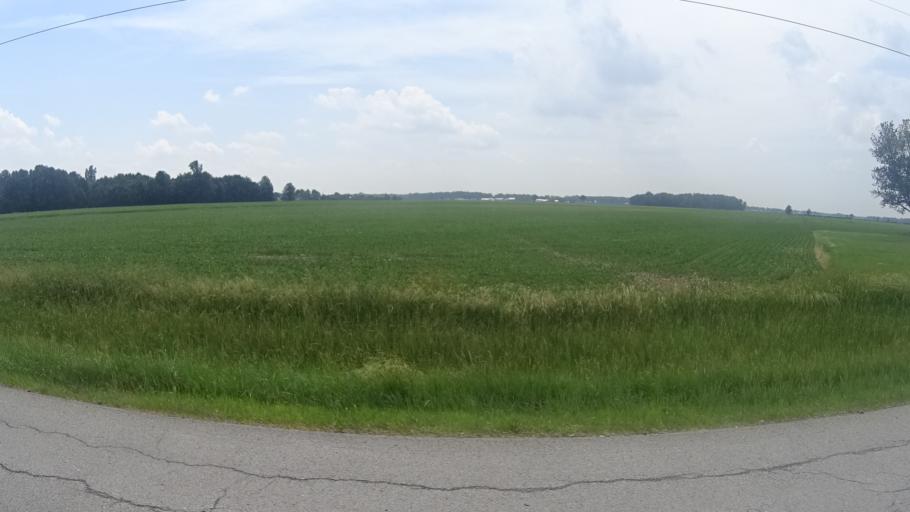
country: US
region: Ohio
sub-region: Erie County
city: Milan
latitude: 41.3144
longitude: -82.6093
